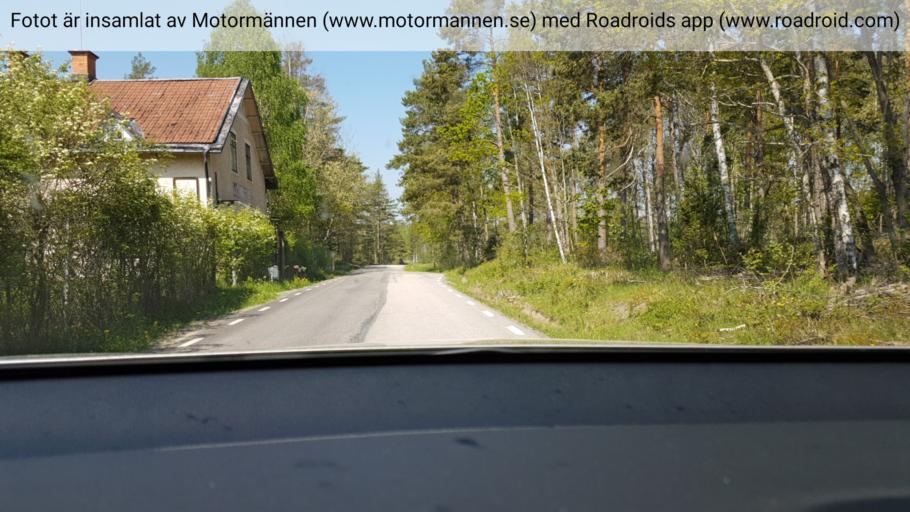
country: SE
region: Kalmar
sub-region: Vasterviks Kommun
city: Gamleby
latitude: 57.8719
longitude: 16.4573
